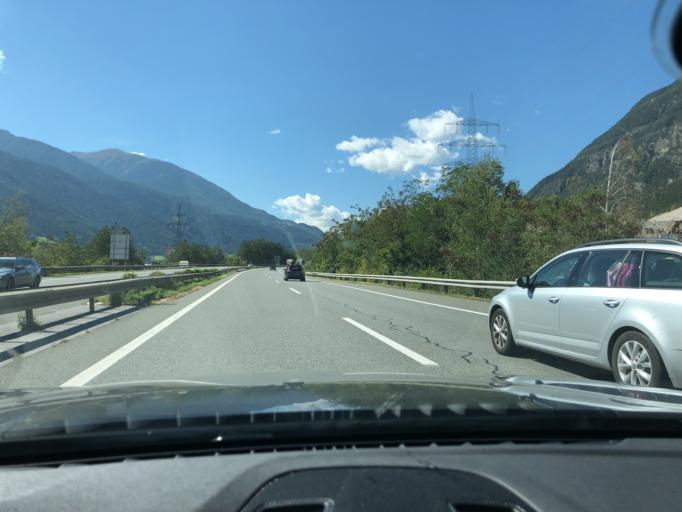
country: AT
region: Tyrol
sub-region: Politischer Bezirk Imst
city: Roppen
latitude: 47.2336
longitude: 10.8353
